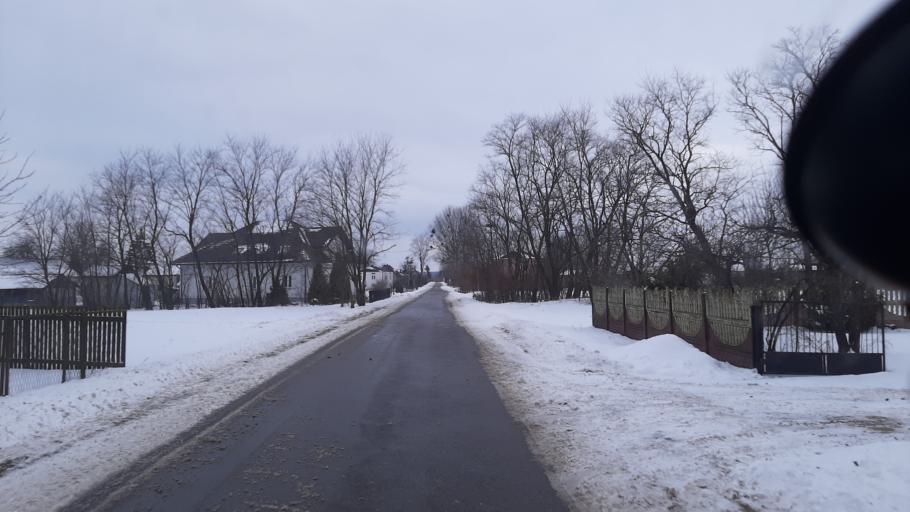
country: PL
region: Lublin Voivodeship
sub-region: Powiat lubartowski
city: Abramow
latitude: 51.4422
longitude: 22.2857
